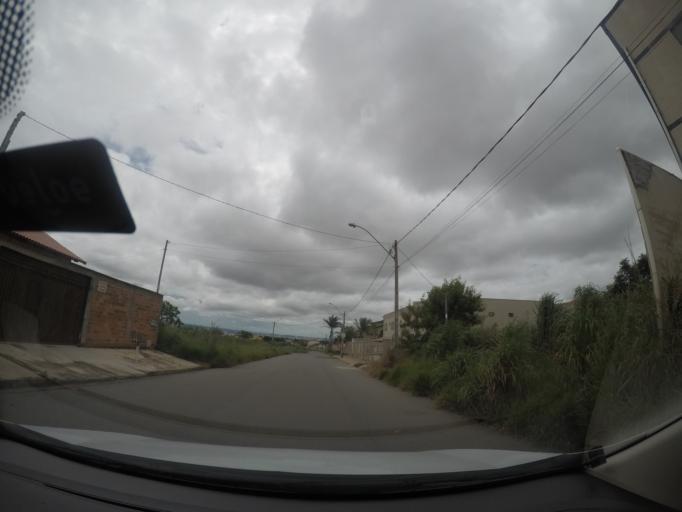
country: BR
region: Goias
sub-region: Goiania
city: Goiania
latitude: -16.7460
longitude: -49.3351
